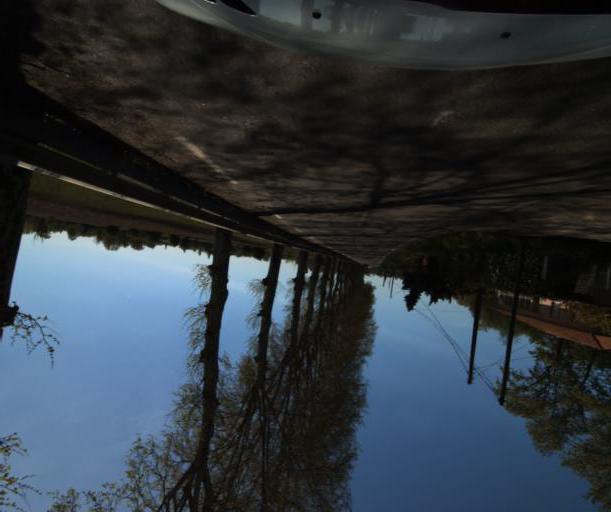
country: FR
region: Midi-Pyrenees
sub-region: Departement du Tarn-et-Garonne
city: Lafrancaise
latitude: 44.0840
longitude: 1.2750
